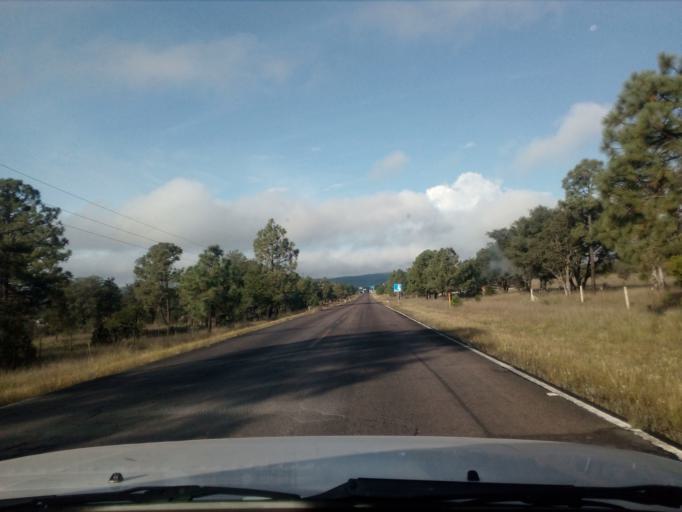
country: MX
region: Durango
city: Victoria de Durango
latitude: 23.9265
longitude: -104.9335
